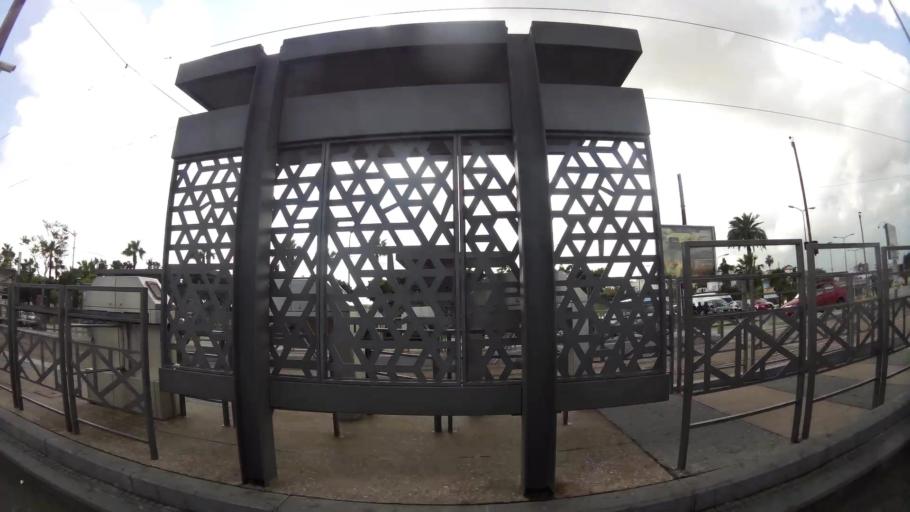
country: MA
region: Grand Casablanca
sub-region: Casablanca
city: Casablanca
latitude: 33.5639
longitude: -7.6275
